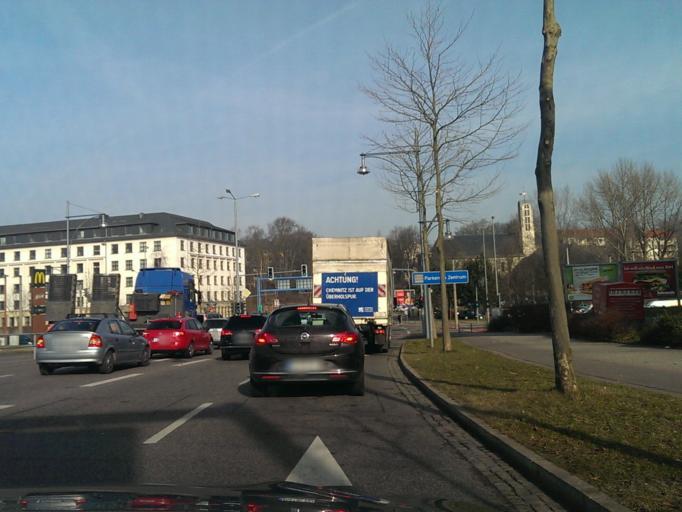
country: DE
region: Saxony
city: Chemnitz
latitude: 50.8272
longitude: 12.9132
